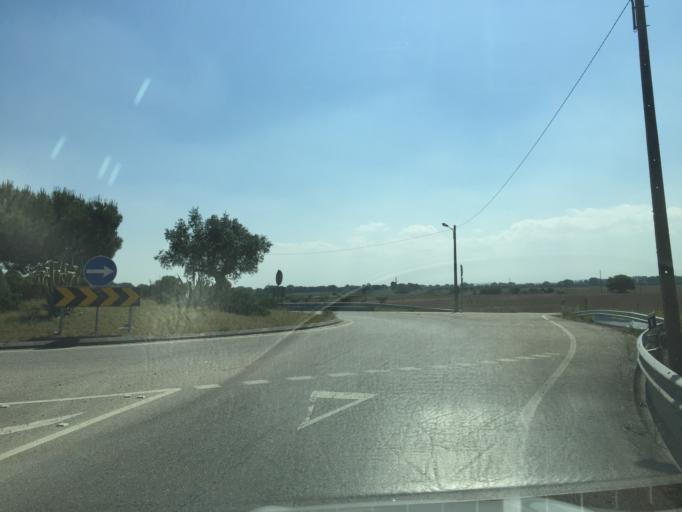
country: PT
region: Santarem
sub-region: Chamusca
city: Vila Nova da Barquinha
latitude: 39.4005
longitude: -8.4338
